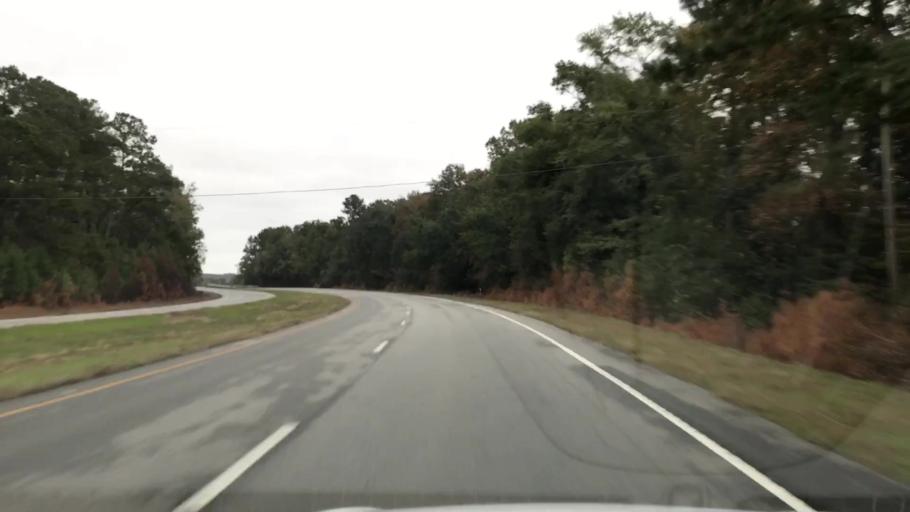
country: US
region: South Carolina
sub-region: Georgetown County
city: Georgetown
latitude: 33.1818
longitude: -79.4084
